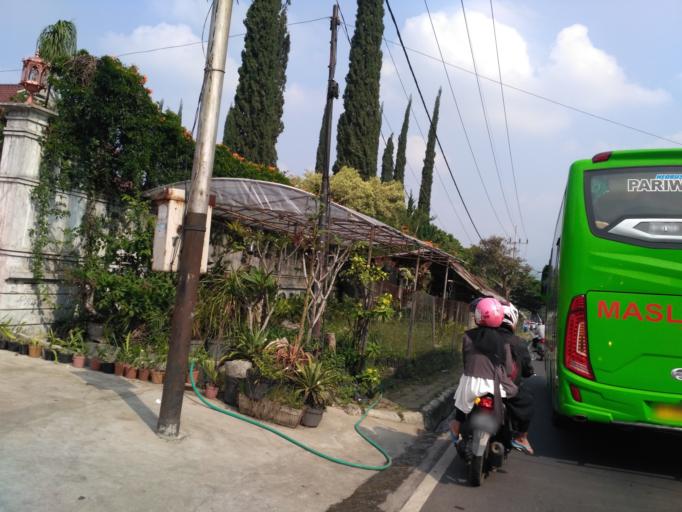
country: ID
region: East Java
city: Batu
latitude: -7.8555
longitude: 112.5271
